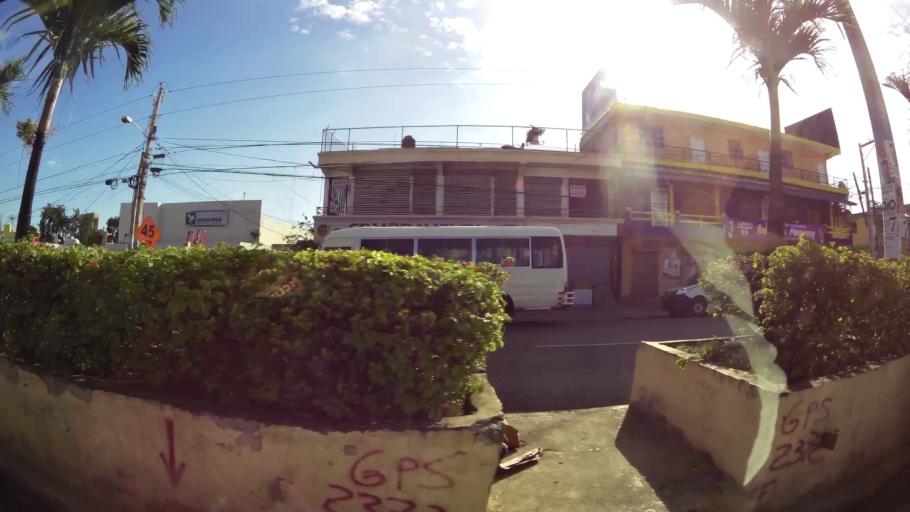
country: DO
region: Santo Domingo
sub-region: Santo Domingo
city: Santo Domingo Este
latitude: 18.4971
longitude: -69.8519
